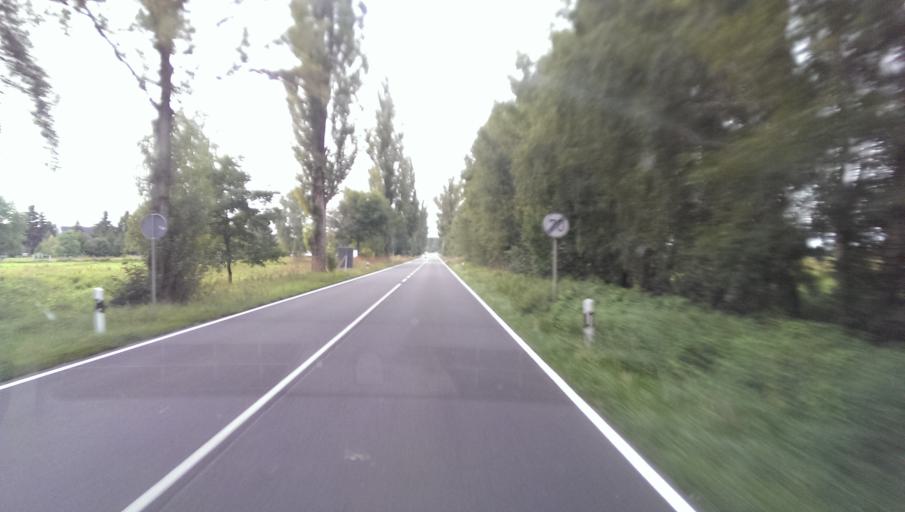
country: DE
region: Saxony-Anhalt
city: Kemberg
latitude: 51.7717
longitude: 12.6437
